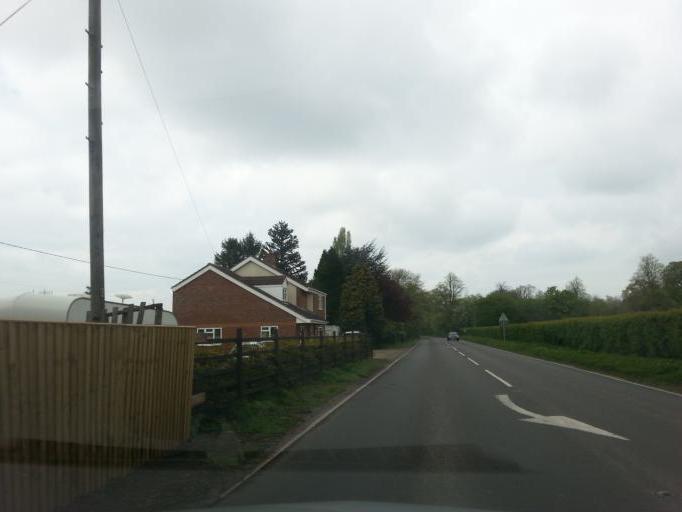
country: GB
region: England
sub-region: Norfolk
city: Emneth
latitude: 52.6372
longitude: 0.1893
